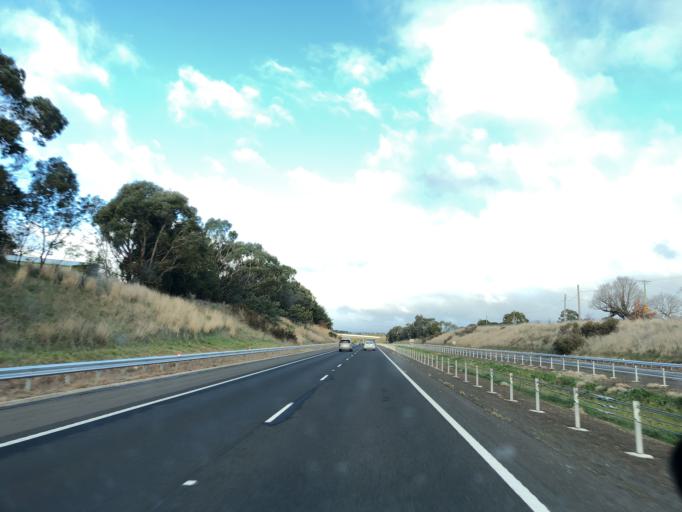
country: AU
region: Victoria
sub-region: Mount Alexander
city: Castlemaine
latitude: -37.2355
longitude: 144.4520
